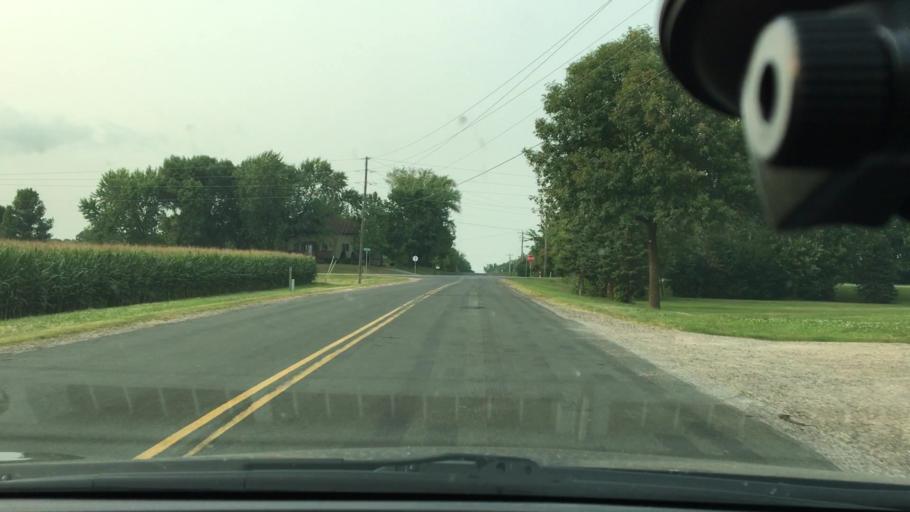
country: US
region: Minnesota
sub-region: Wright County
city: Albertville
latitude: 45.2893
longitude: -93.6839
